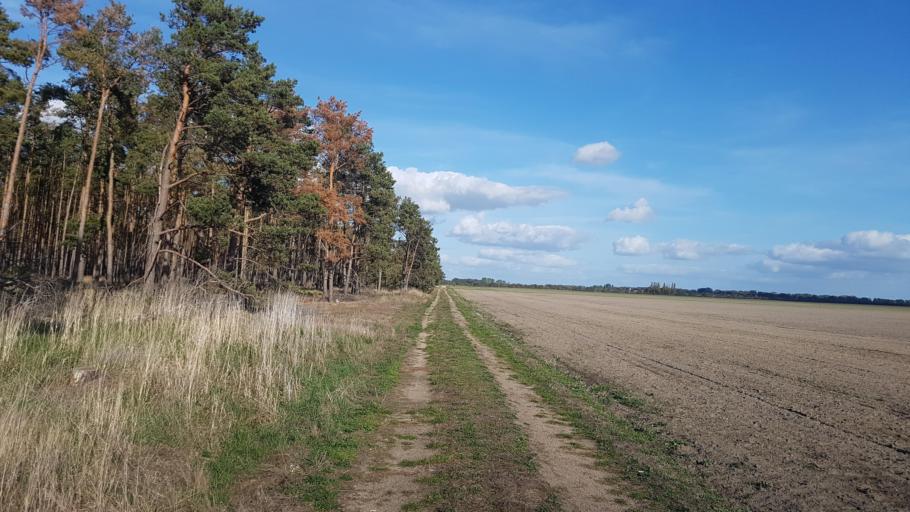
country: DE
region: Brandenburg
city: Muhlberg
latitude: 51.4495
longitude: 13.3055
